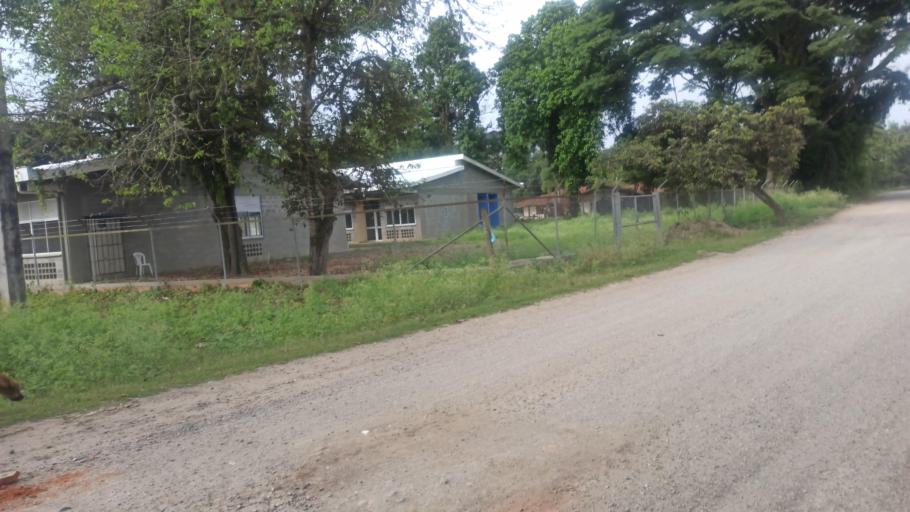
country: CO
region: Valle del Cauca
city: Jamundi
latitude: 3.2020
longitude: -76.5011
